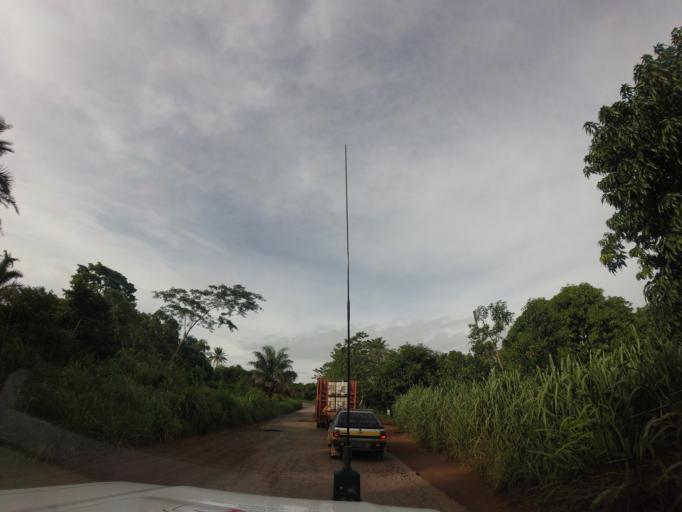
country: GN
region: Kindia
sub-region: Kindia
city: Kindia
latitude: 9.9176
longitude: -12.9971
